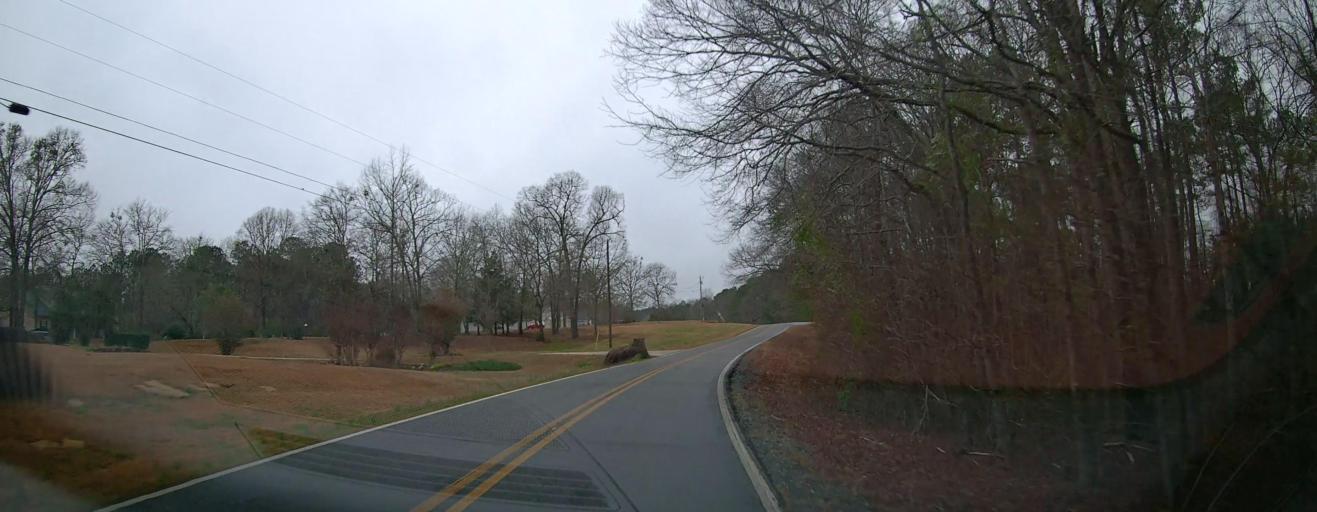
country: US
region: Georgia
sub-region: Monroe County
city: Forsyth
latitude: 33.1153
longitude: -83.9550
